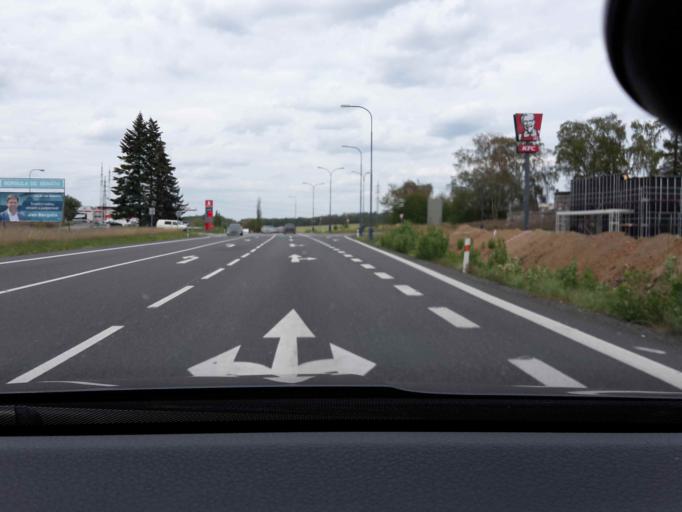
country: CZ
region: Central Bohemia
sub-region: Okres Benesov
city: Benesov
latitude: 49.7929
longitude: 14.6792
